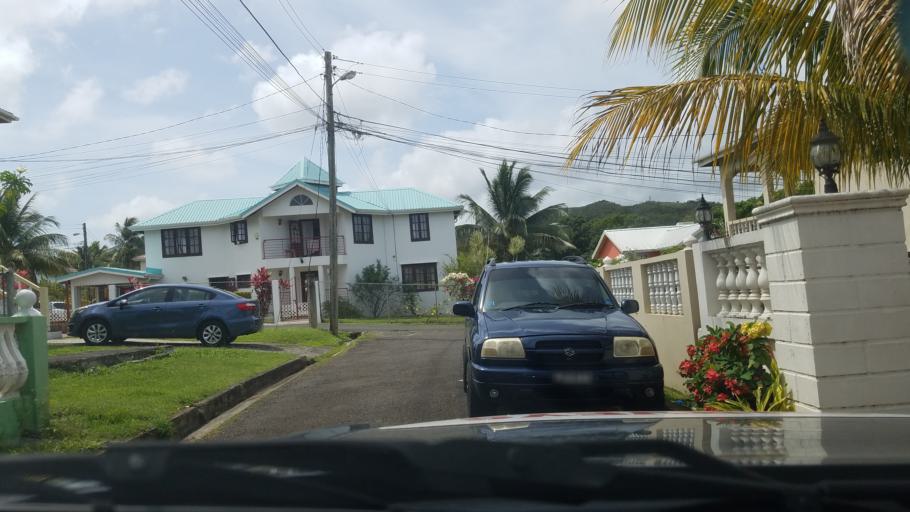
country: LC
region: Gros-Islet
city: Gros Islet
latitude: 14.0453
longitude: -60.9614
